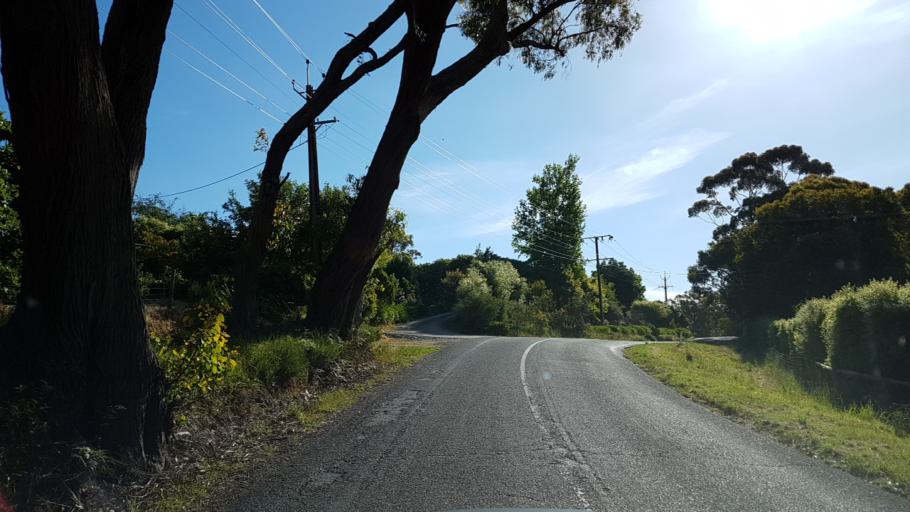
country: AU
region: South Australia
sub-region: Adelaide Hills
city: Adelaide Hills
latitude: -34.9387
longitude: 138.7409
